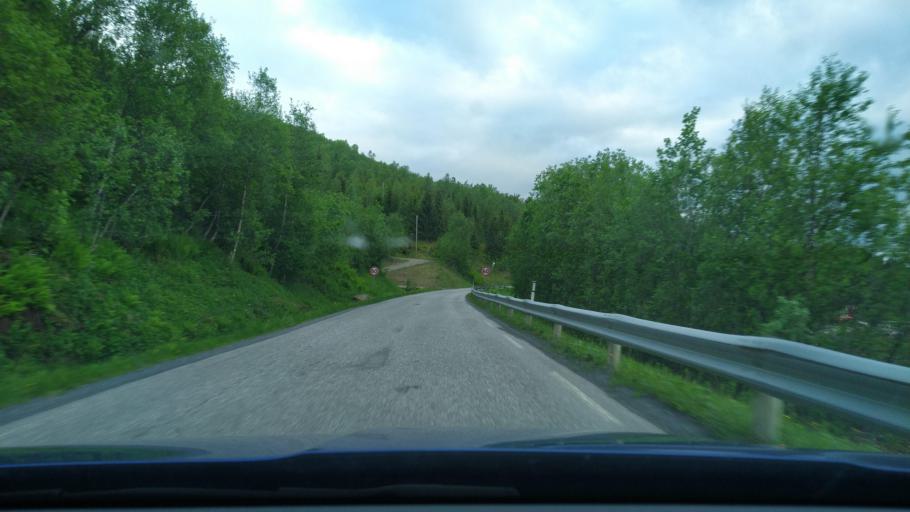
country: NO
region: Troms
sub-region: Lenvik
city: Finnsnes
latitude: 69.1378
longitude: 17.9061
